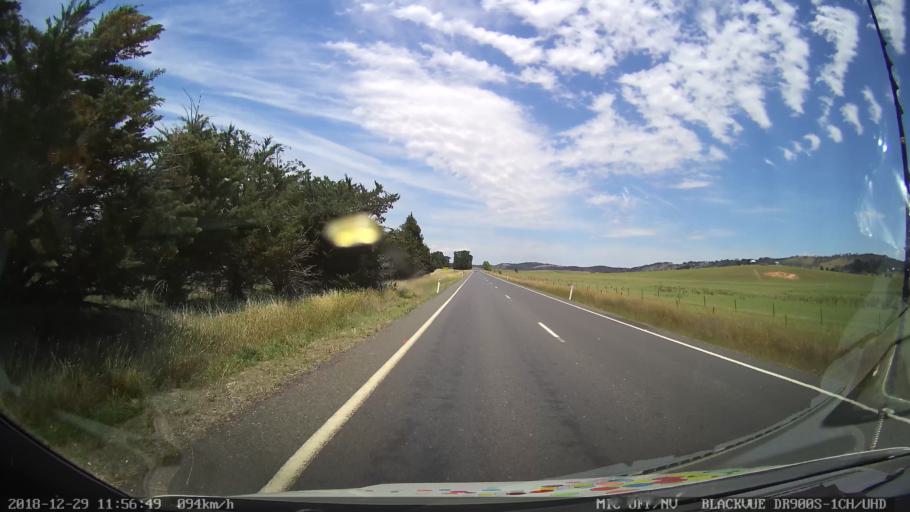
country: AU
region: New South Wales
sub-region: Palerang
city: Bungendore
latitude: -35.2809
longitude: 149.4224
